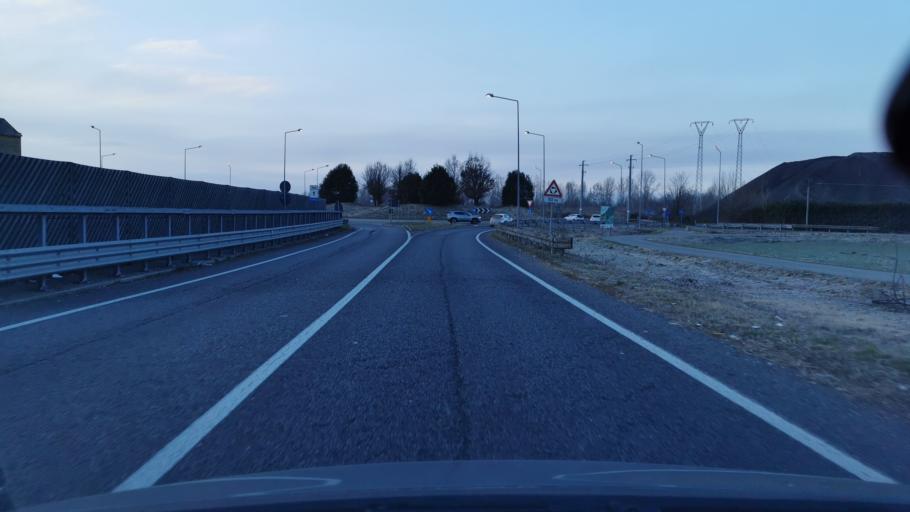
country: IT
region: Piedmont
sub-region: Provincia di Torino
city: Borgaro Torinese
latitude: 45.1547
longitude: 7.6446
